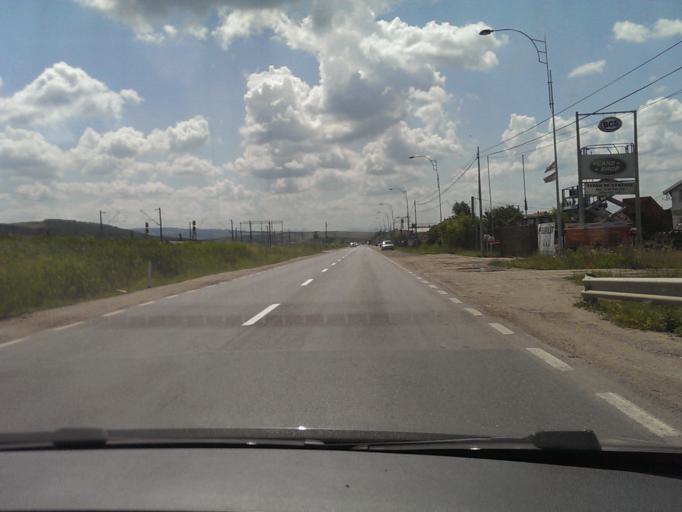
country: RO
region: Cluj
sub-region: Comuna Apahida
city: Sannicoara
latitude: 46.7880
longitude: 23.7301
